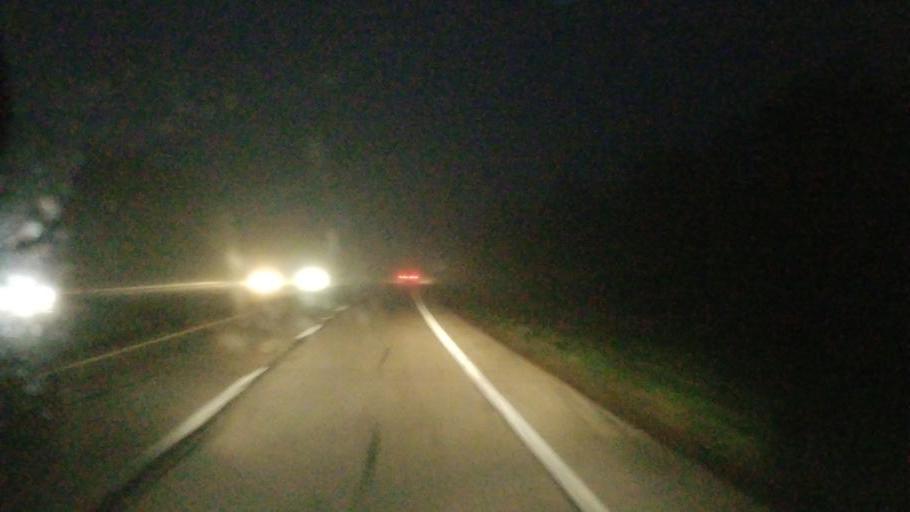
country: US
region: Ohio
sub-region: Ross County
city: Kingston
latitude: 39.4908
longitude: -82.9721
